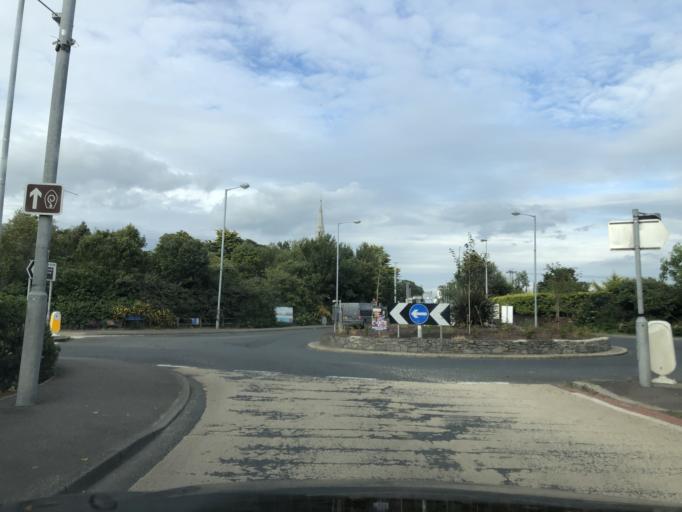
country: GB
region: Northern Ireland
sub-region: Down District
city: Castlewellan
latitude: 54.2556
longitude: -5.9489
